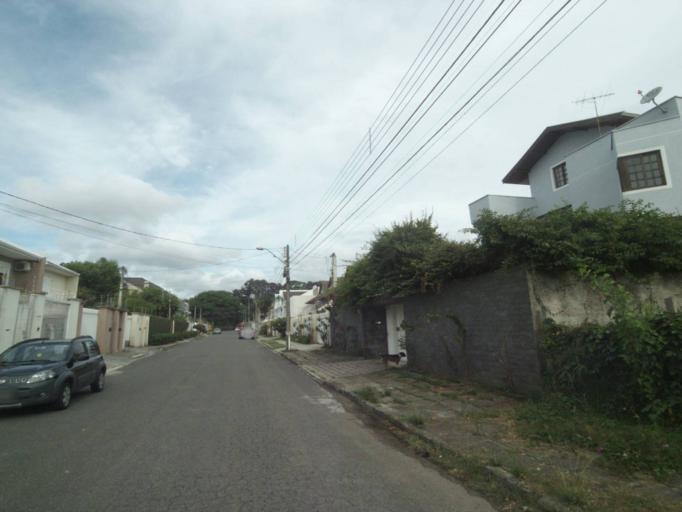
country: BR
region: Parana
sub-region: Curitiba
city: Curitiba
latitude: -25.4410
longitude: -49.3161
